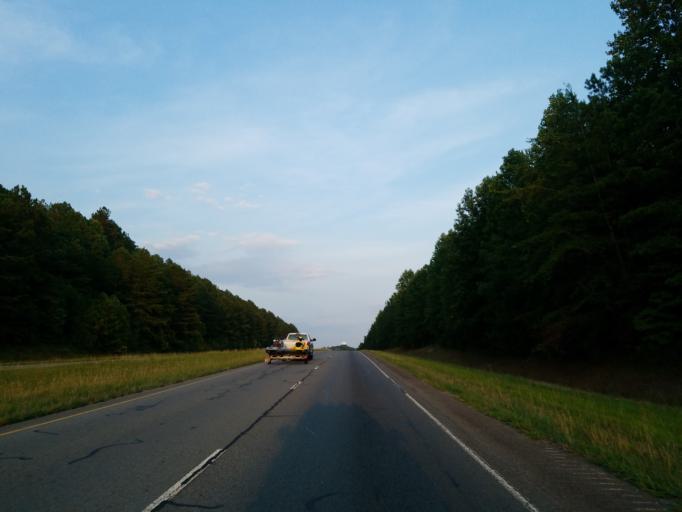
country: US
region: Georgia
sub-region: Pickens County
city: Jasper
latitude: 34.4943
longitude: -84.4881
